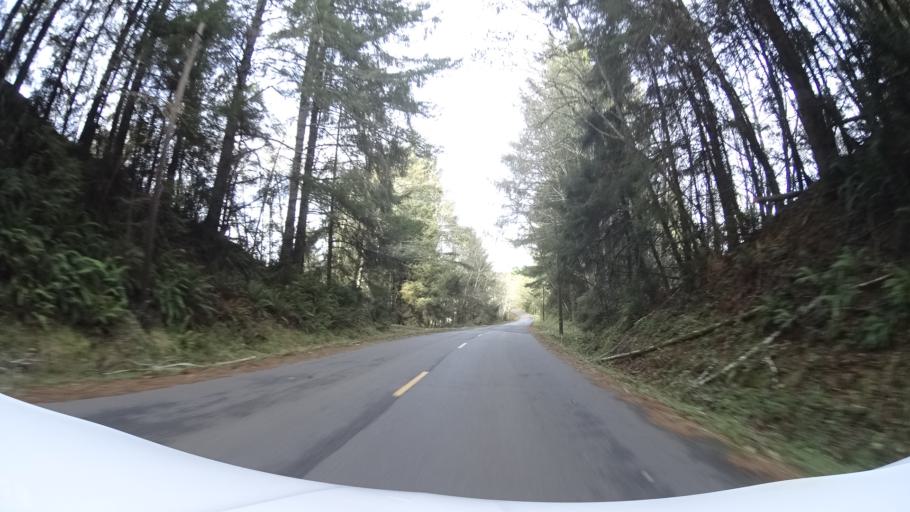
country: US
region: California
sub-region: Humboldt County
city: Ferndale
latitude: 40.5557
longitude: -124.2736
